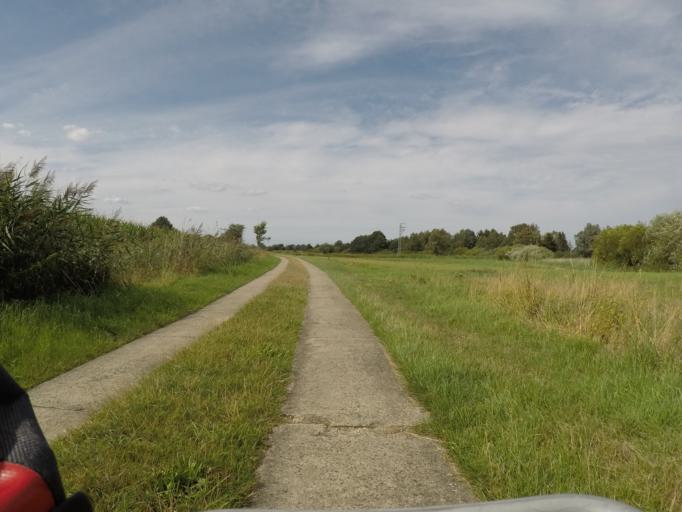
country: DE
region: Lower Saxony
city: Drage
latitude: 53.3690
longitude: 10.2773
